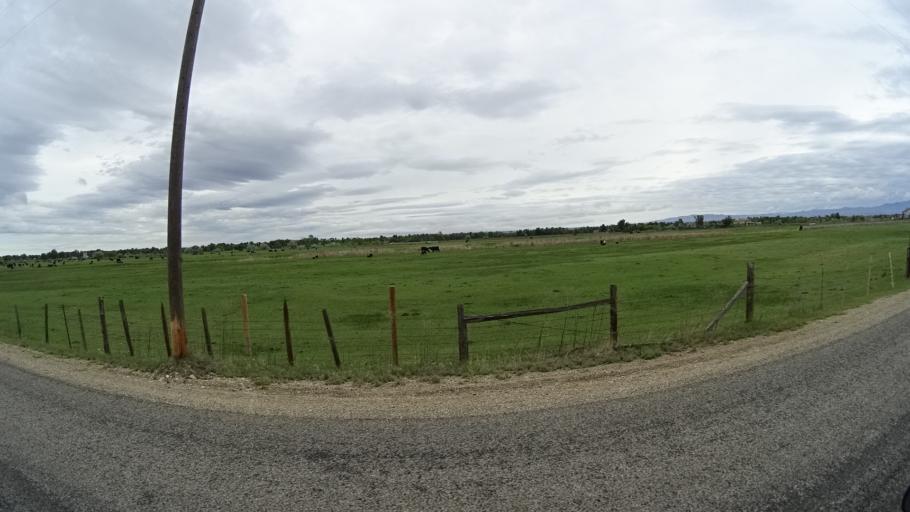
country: US
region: Idaho
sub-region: Ada County
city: Star
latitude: 43.6701
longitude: -116.4837
